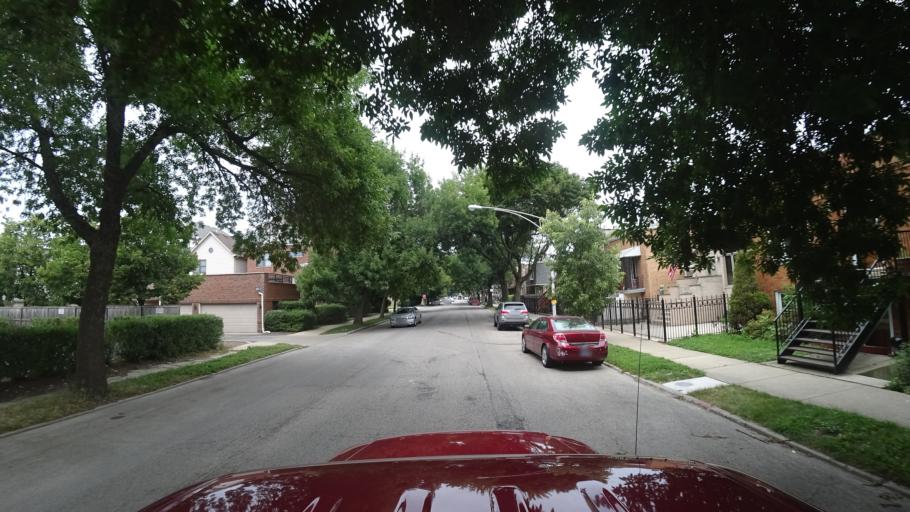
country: US
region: Illinois
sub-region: Cook County
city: Chicago
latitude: 41.8327
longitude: -87.6559
